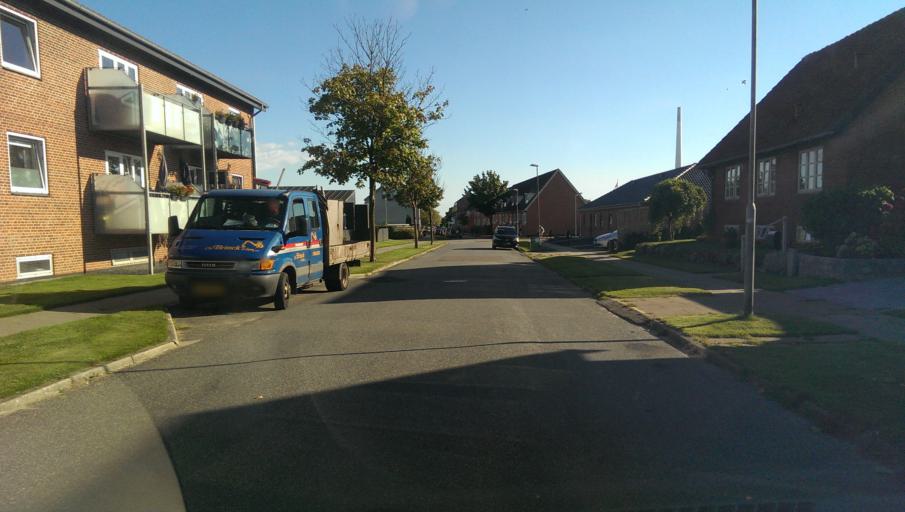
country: DK
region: South Denmark
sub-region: Esbjerg Kommune
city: Esbjerg
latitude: 55.4675
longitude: 8.4643
